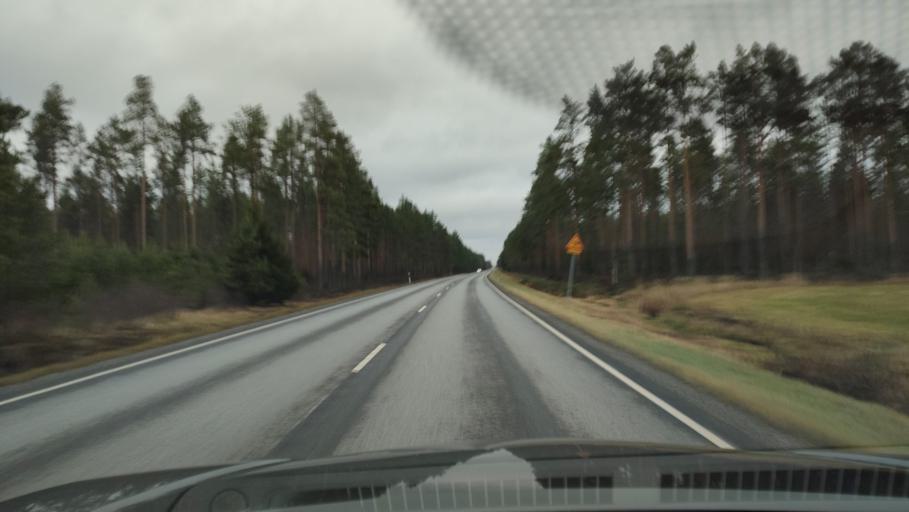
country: FI
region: Southern Ostrobothnia
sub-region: Seinaejoki
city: Kurikka
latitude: 62.5151
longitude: 22.3129
